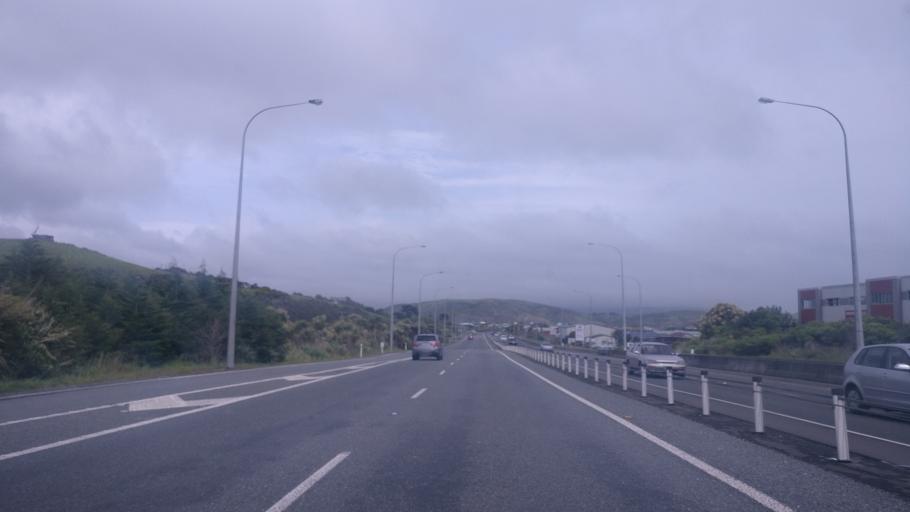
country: NZ
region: Wellington
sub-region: Porirua City
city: Porirua
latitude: -41.0774
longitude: 174.8734
